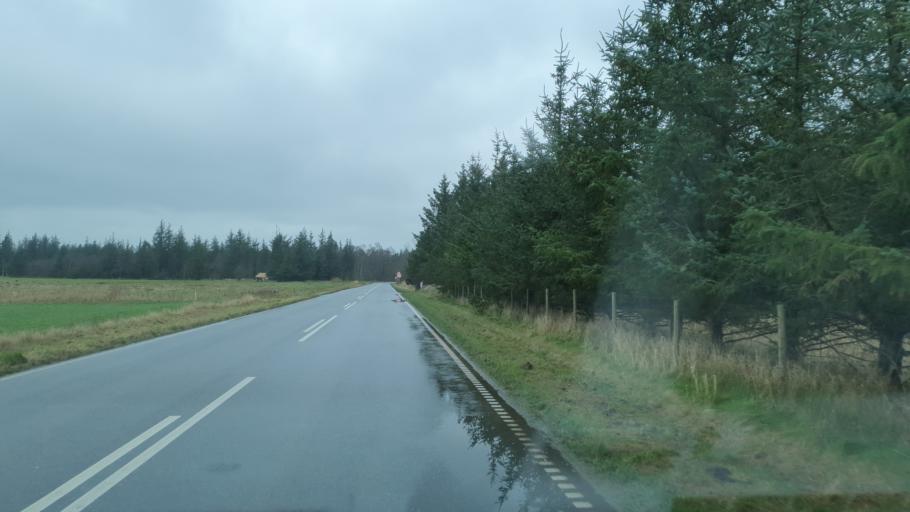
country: DK
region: North Denmark
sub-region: Jammerbugt Kommune
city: Fjerritslev
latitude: 57.1163
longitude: 9.1274
